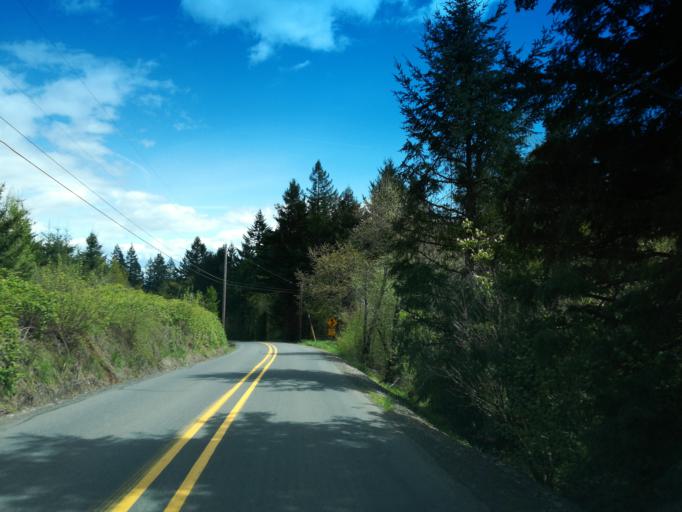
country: US
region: Oregon
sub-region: Clackamas County
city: Damascus
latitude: 45.4507
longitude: -122.4471
